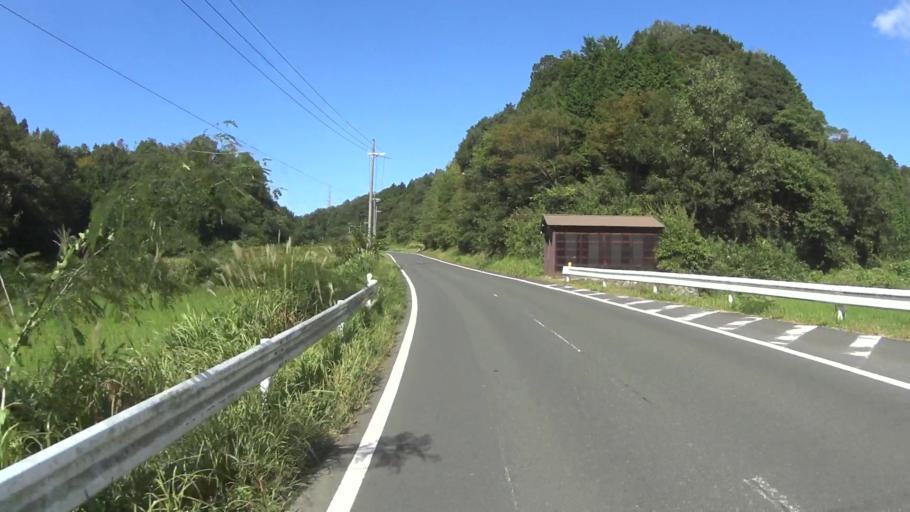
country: JP
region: Kyoto
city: Miyazu
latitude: 35.6585
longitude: 135.0659
